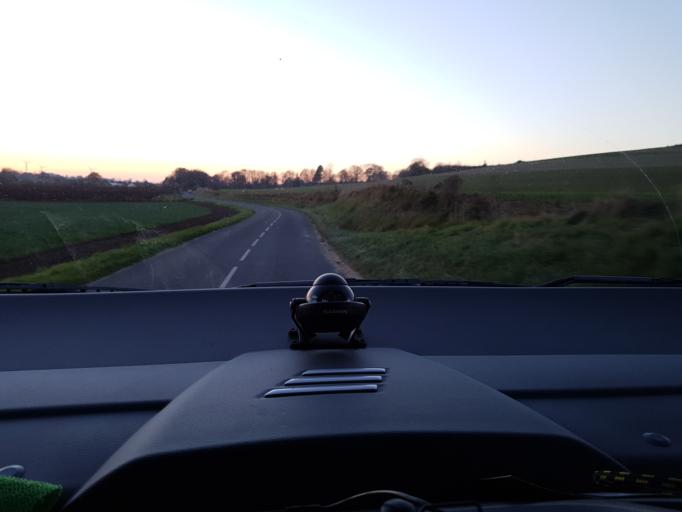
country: FR
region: Picardie
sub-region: Departement de la Somme
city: Rue
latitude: 50.3209
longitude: 1.7760
